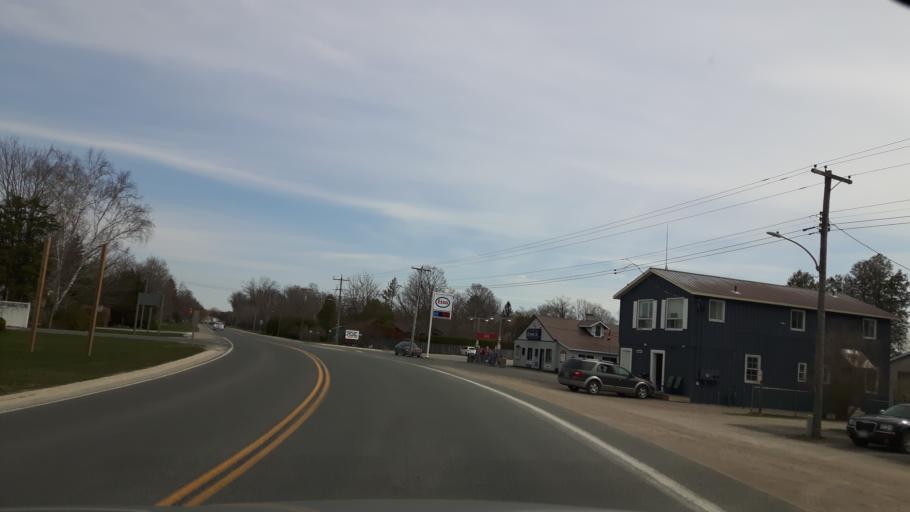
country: CA
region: Ontario
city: Bluewater
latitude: 43.5616
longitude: -81.6967
